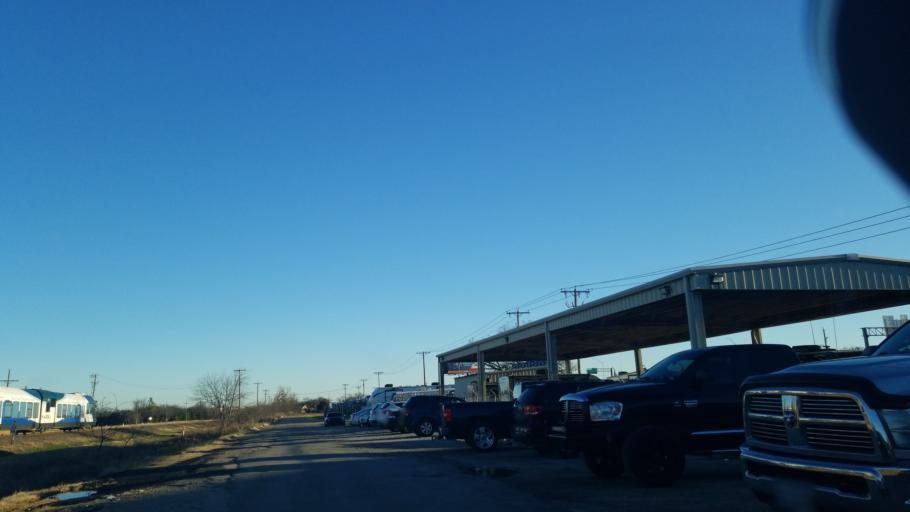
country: US
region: Texas
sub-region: Denton County
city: Corinth
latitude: 33.1581
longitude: -97.0650
